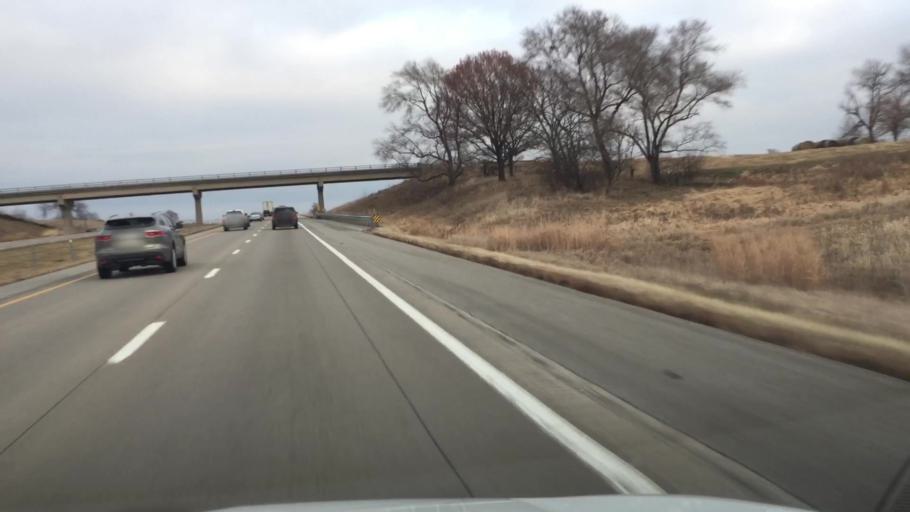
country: US
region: Iowa
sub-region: Jasper County
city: Newton
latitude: 41.6813
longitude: -93.1179
